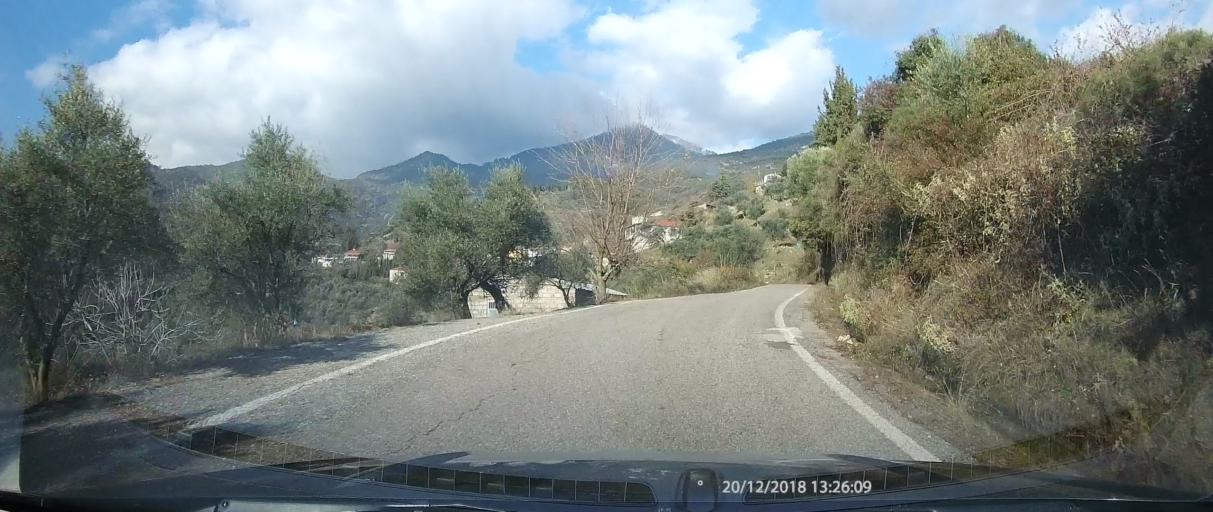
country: GR
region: West Greece
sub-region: Nomos Aitolias kai Akarnanias
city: Paravola
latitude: 38.6273
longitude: 21.5648
